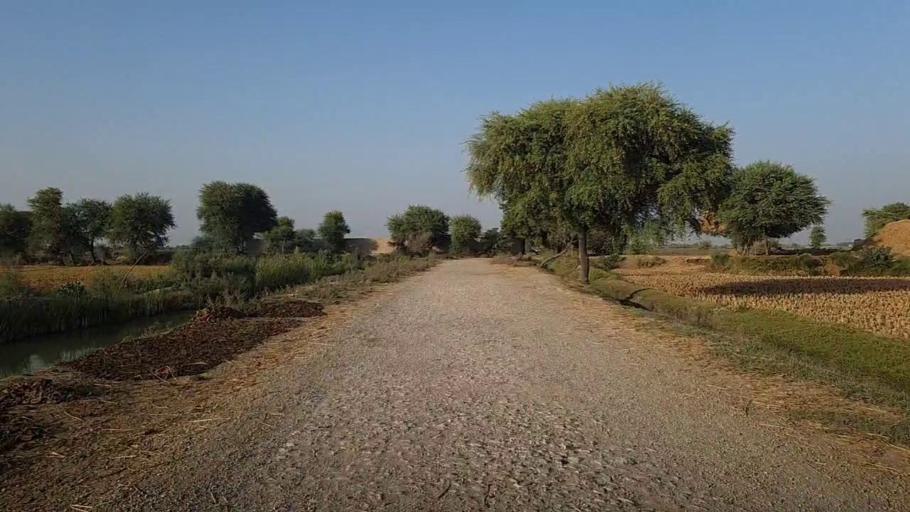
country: PK
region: Sindh
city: Kashmor
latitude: 28.4285
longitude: 69.4427
